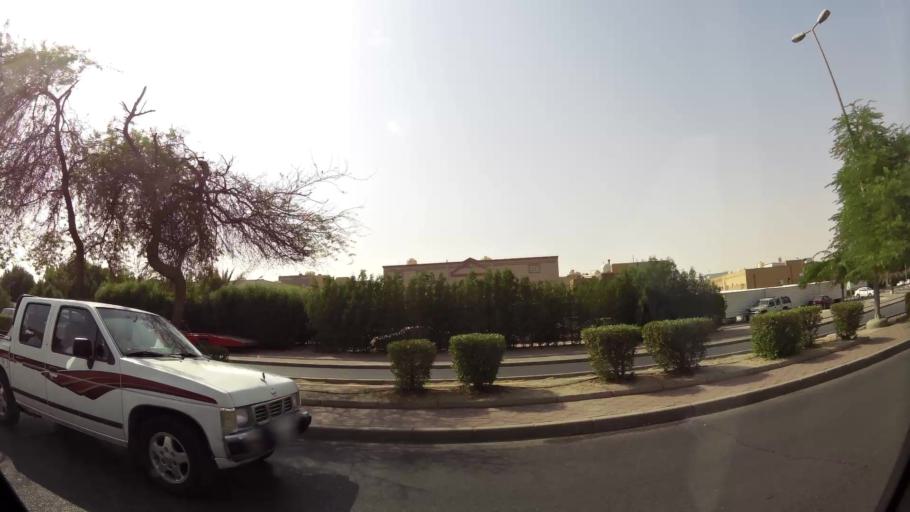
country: KW
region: Muhafazat al Jahra'
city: Al Jahra'
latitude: 29.3409
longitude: 47.6676
